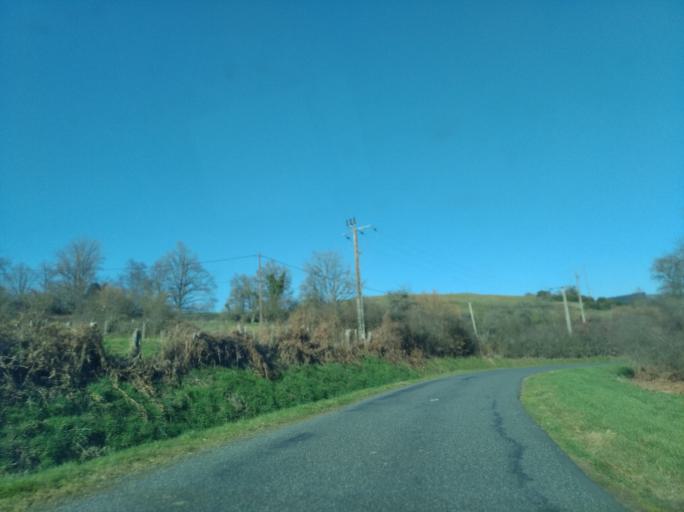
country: FR
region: Auvergne
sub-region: Departement de l'Allier
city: Le Mayet-de-Montagne
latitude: 46.0853
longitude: 3.6765
